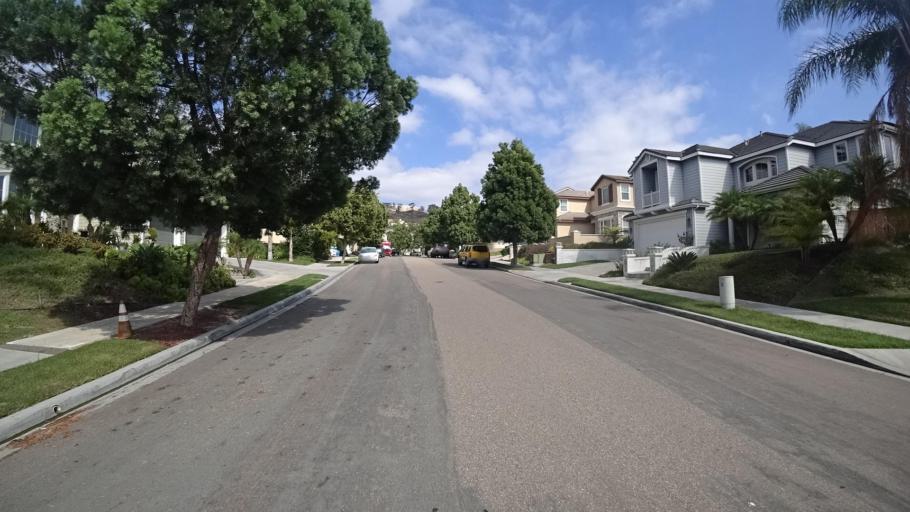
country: US
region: California
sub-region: San Diego County
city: Fairbanks Ranch
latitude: 33.0076
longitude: -117.1074
